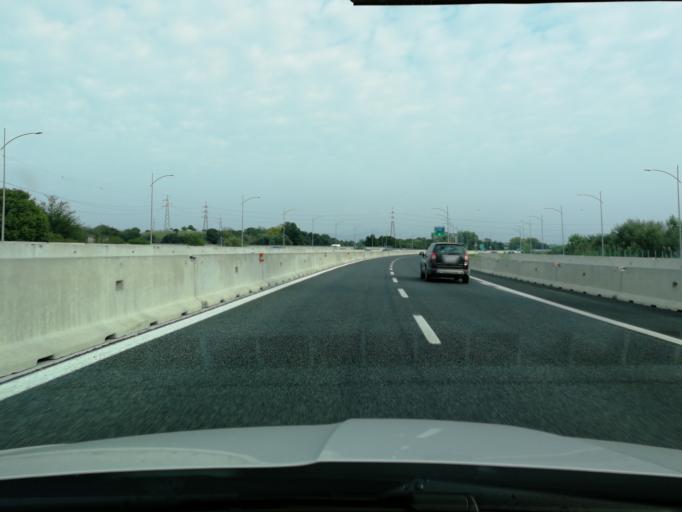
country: IT
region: Latium
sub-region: Citta metropolitana di Roma Capitale
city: Setteville
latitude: 41.9236
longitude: 12.6433
